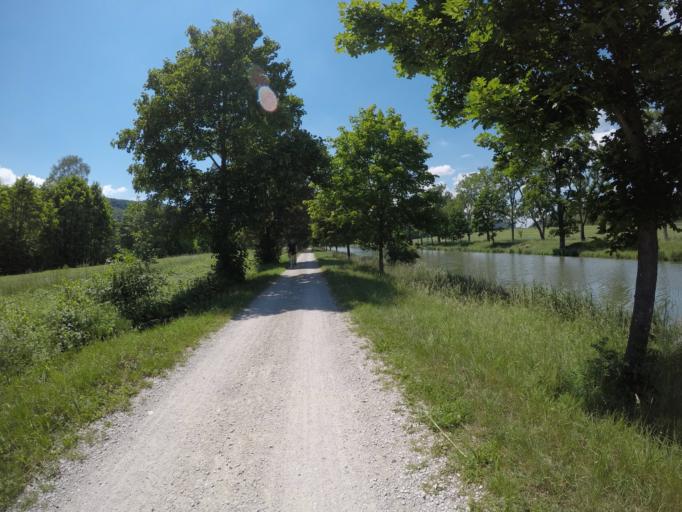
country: DE
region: Bavaria
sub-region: Lower Bavaria
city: Essing
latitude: 48.9259
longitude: 11.8119
